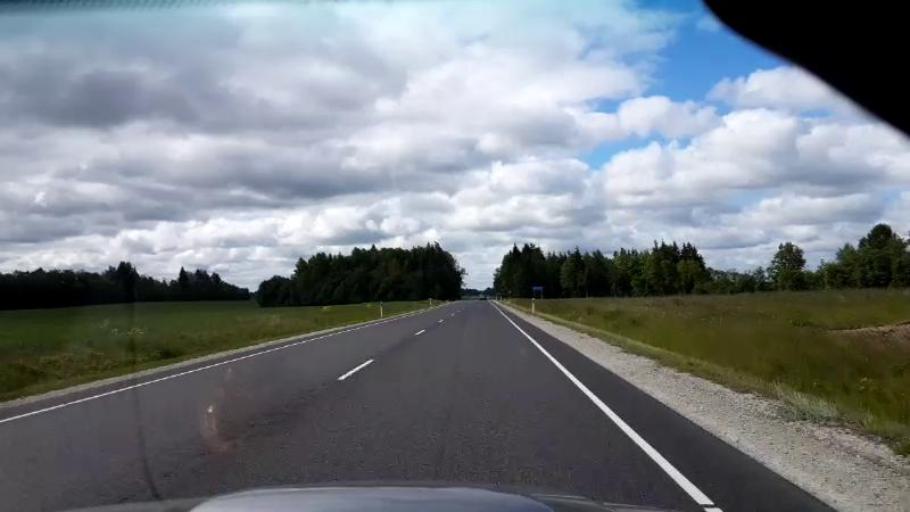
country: EE
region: Raplamaa
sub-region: Maerjamaa vald
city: Marjamaa
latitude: 58.8564
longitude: 24.4336
